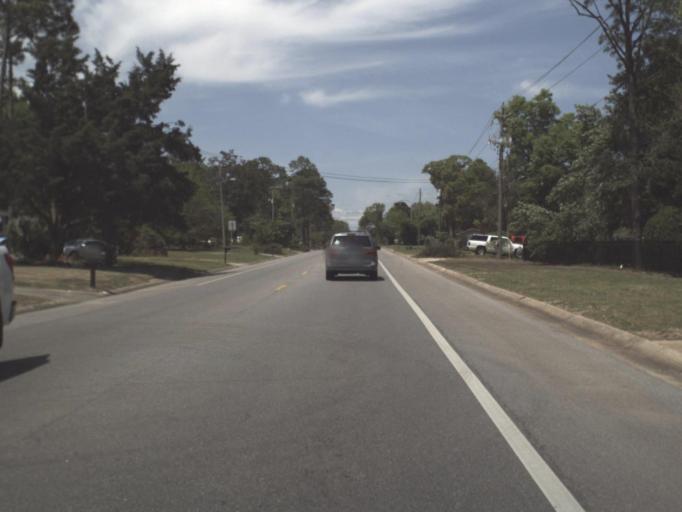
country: US
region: Florida
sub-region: Escambia County
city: Goulding
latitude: 30.4568
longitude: -87.1971
